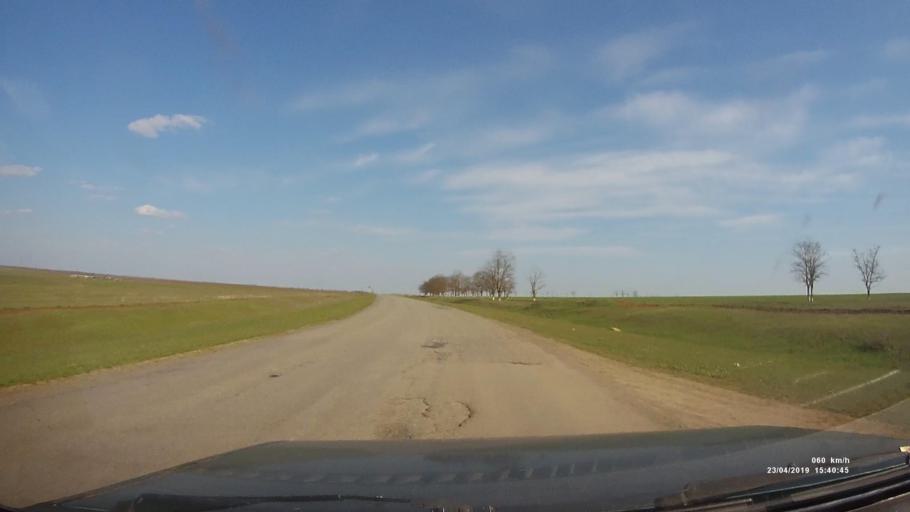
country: RU
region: Rostov
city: Remontnoye
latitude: 46.5538
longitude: 43.0415
